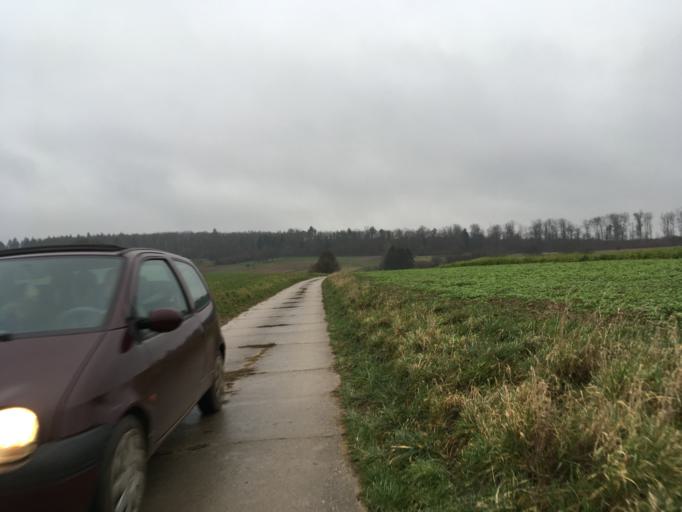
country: DE
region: Baden-Wuerttemberg
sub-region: Karlsruhe Region
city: Konigsbach-Stein
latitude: 48.9627
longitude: 8.5166
